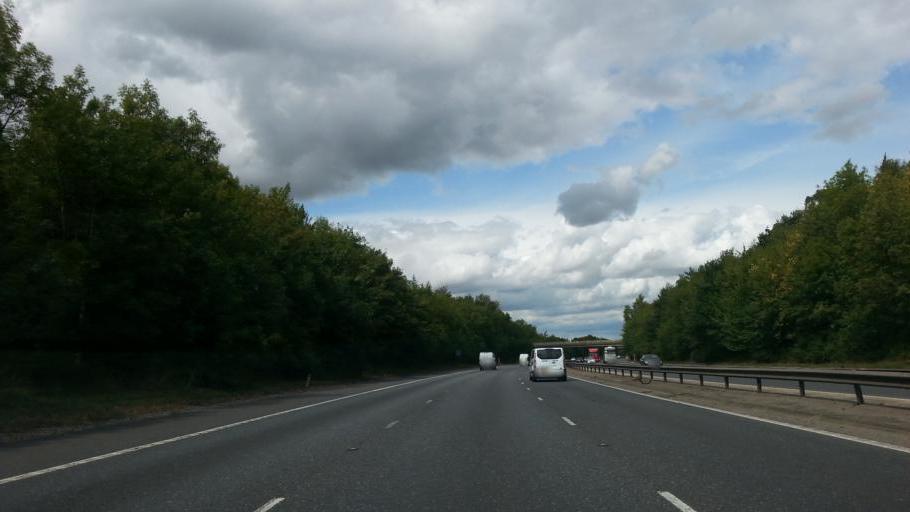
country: GB
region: England
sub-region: Essex
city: Little Hallingbury
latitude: 51.8474
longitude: 0.1856
